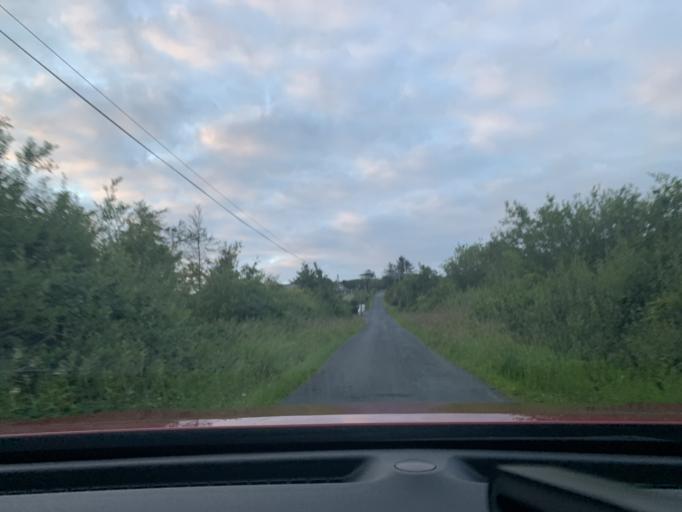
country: IE
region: Connaught
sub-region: Sligo
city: Sligo
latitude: 54.3561
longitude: -8.5059
